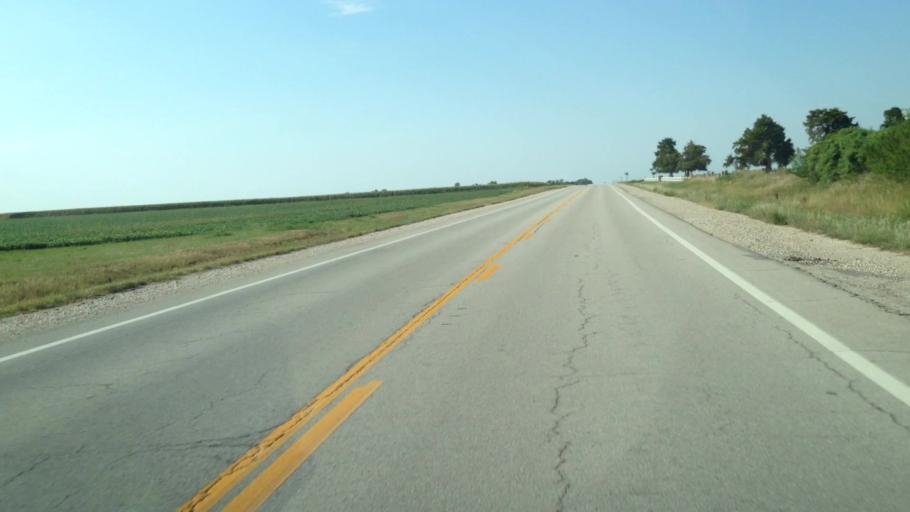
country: US
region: Kansas
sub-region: Anderson County
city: Garnett
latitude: 38.0862
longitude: -95.2434
